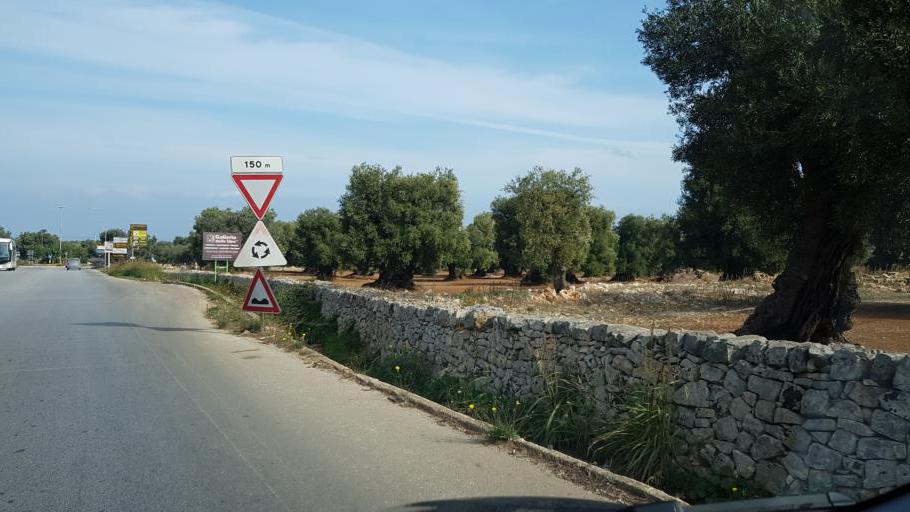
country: IT
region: Apulia
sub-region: Provincia di Brindisi
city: Ostuni
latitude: 40.7426
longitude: 17.5789
